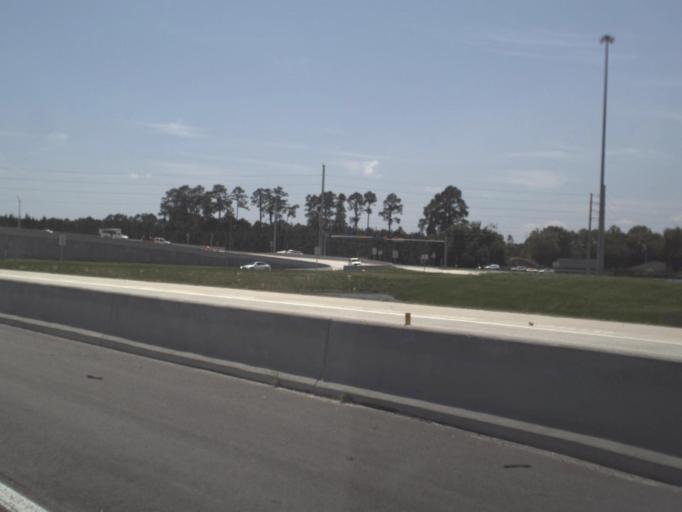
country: US
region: Florida
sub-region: Clay County
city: Bellair-Meadowbrook Terrace
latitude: 30.2065
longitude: -81.7576
